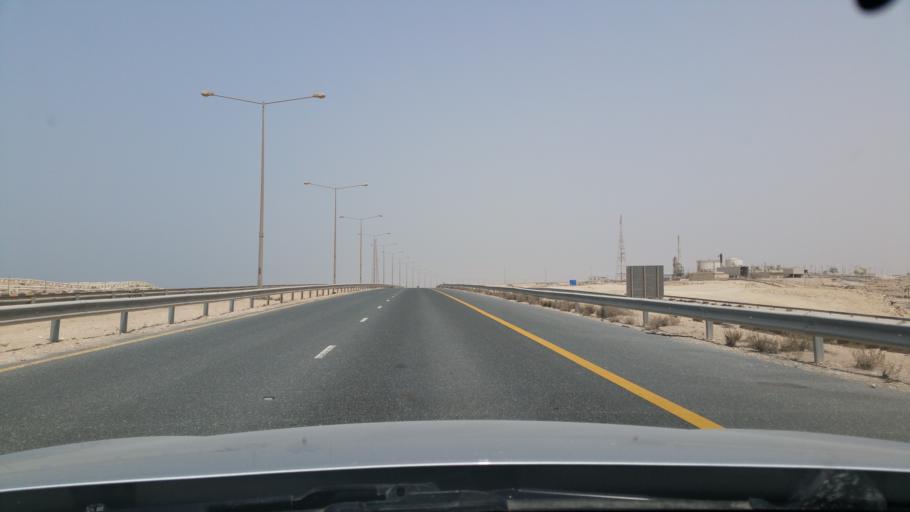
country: QA
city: Umm Bab
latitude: 25.2811
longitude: 50.7913
